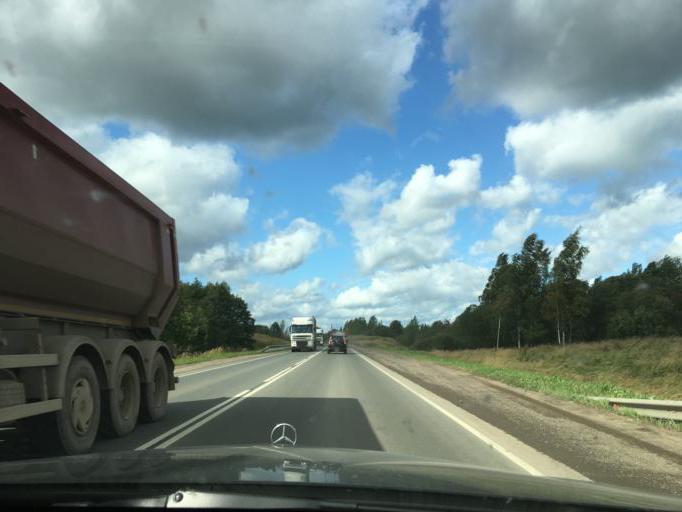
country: RU
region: Pskov
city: Novosokol'niki
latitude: 56.2984
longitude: 30.2225
